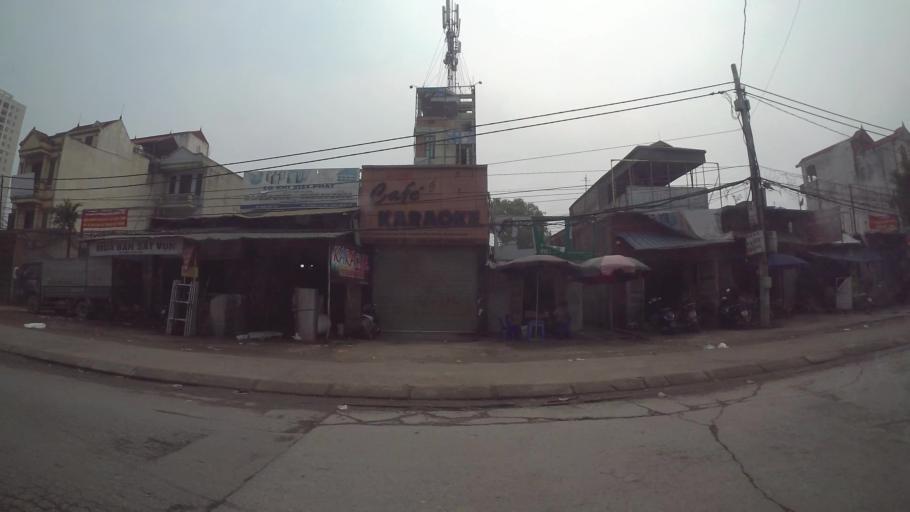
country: VN
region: Ha Noi
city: Van Dien
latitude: 20.9655
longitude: 105.8683
